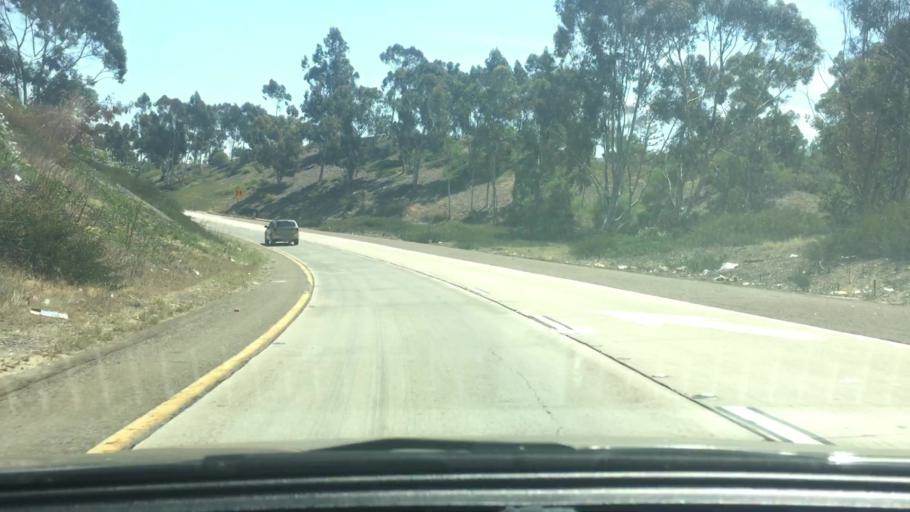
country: US
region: California
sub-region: San Diego County
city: National City
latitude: 32.7184
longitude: -117.1042
